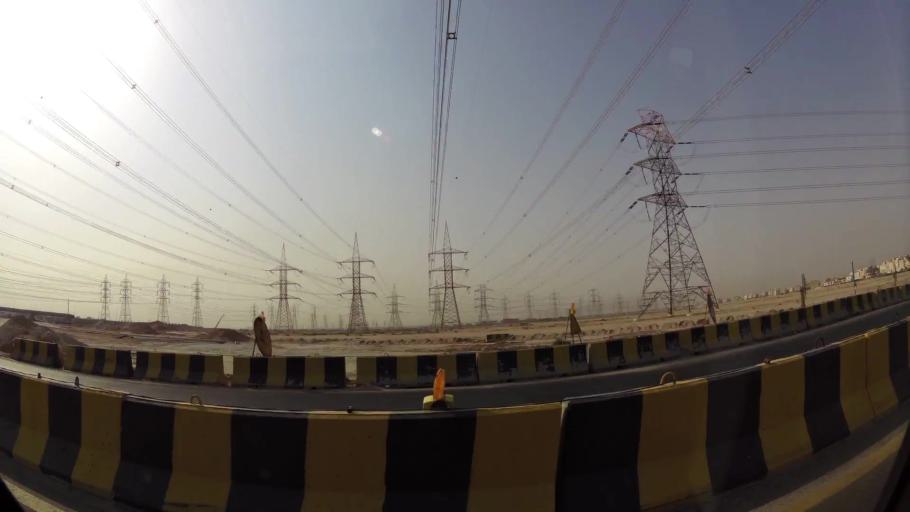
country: KW
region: Muhafazat al Jahra'
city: Al Jahra'
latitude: 29.3391
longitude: 47.7938
